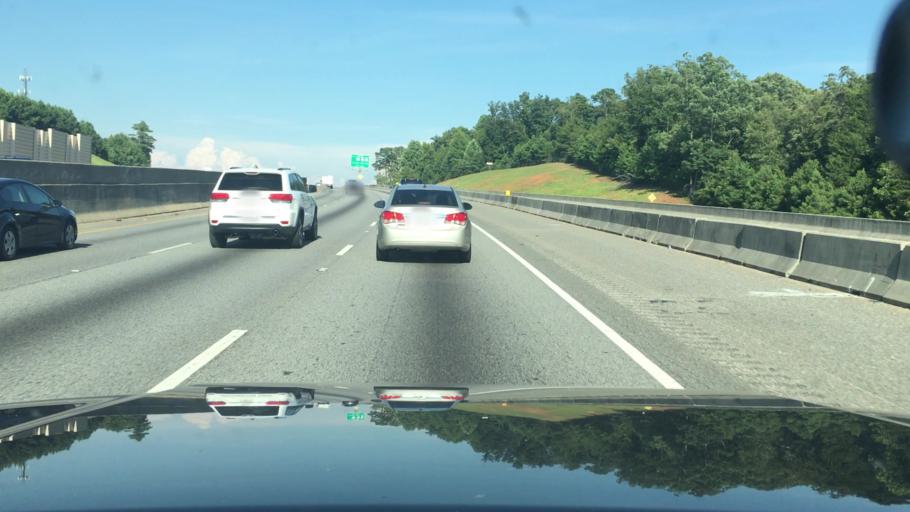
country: US
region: Georgia
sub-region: DeKalb County
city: Lithonia
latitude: 33.7015
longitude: -84.1135
